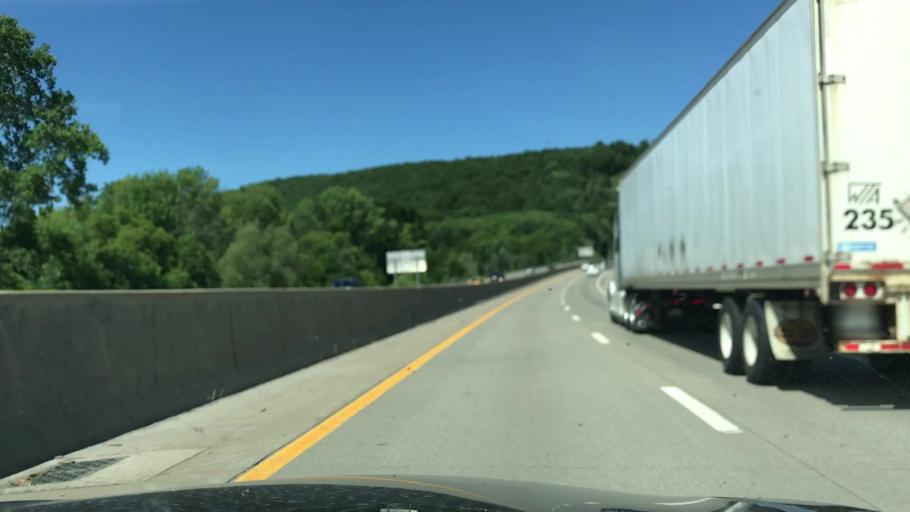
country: US
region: New York
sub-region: Steuben County
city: Painted Post
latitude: 42.1607
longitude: -77.0735
